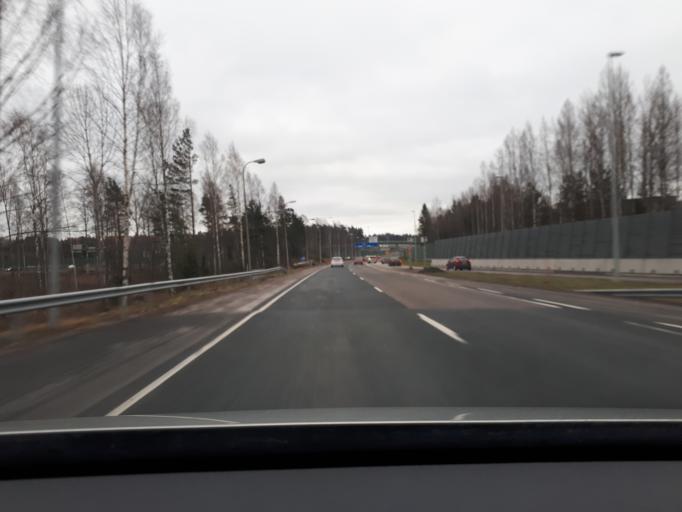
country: FI
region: Uusimaa
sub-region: Helsinki
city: Vantaa
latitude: 60.2360
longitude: 25.0437
